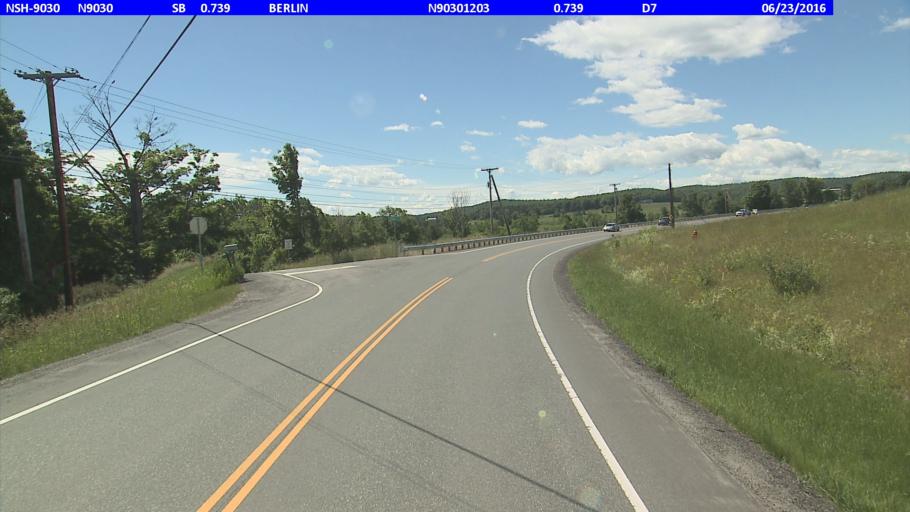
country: US
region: Vermont
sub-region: Washington County
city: Montpelier
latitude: 44.2125
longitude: -72.5553
